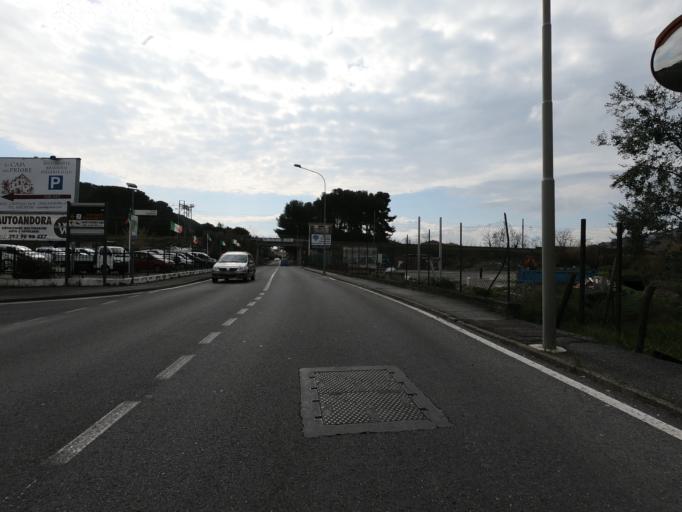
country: IT
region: Liguria
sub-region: Provincia di Savona
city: Andora
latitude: 43.9628
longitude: 8.1421
